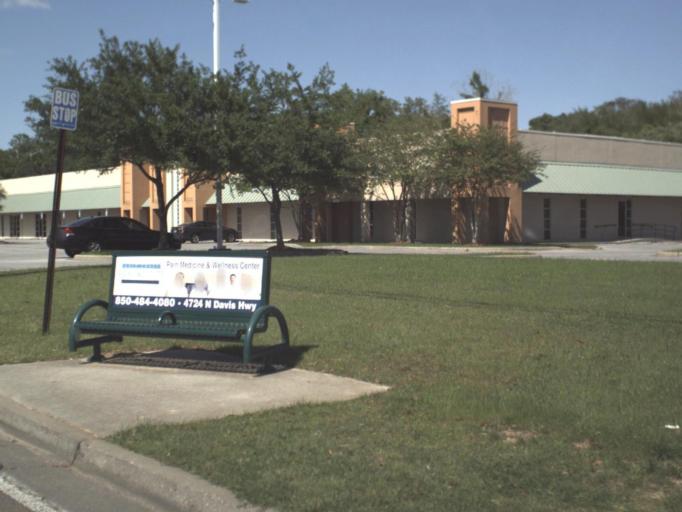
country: US
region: Florida
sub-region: Escambia County
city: Brent
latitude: 30.4699
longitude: -87.2248
